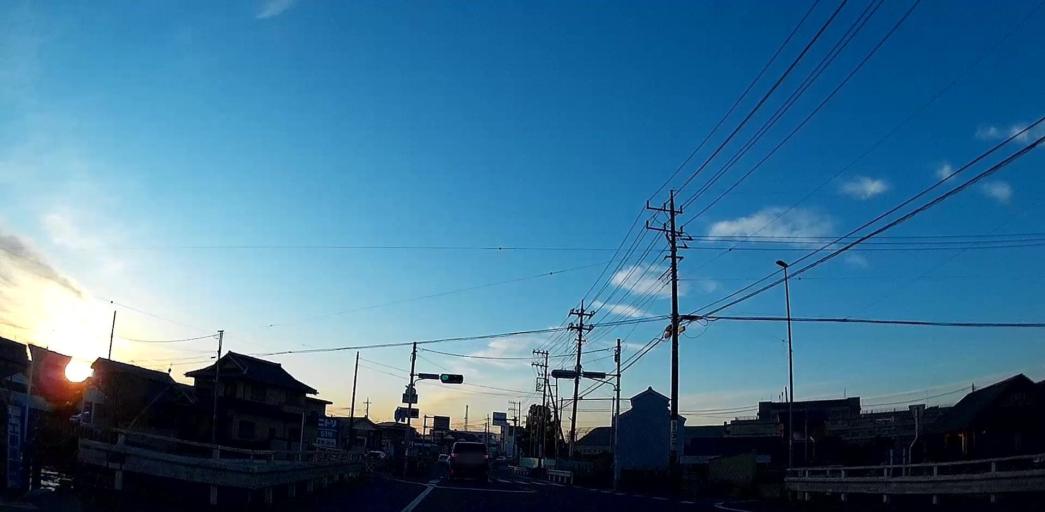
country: JP
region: Chiba
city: Katori-shi
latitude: 35.8956
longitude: 140.5024
